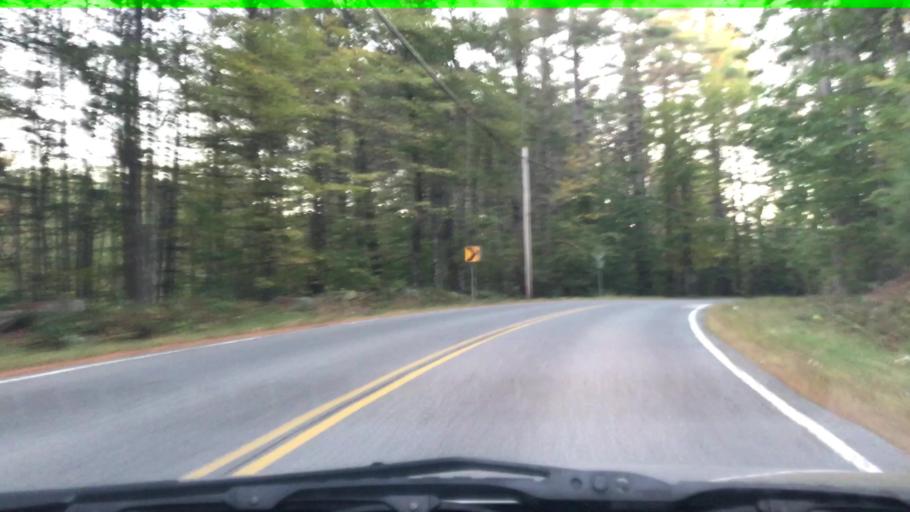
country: US
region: New Hampshire
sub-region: Cheshire County
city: Swanzey
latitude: 42.8887
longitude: -72.2868
